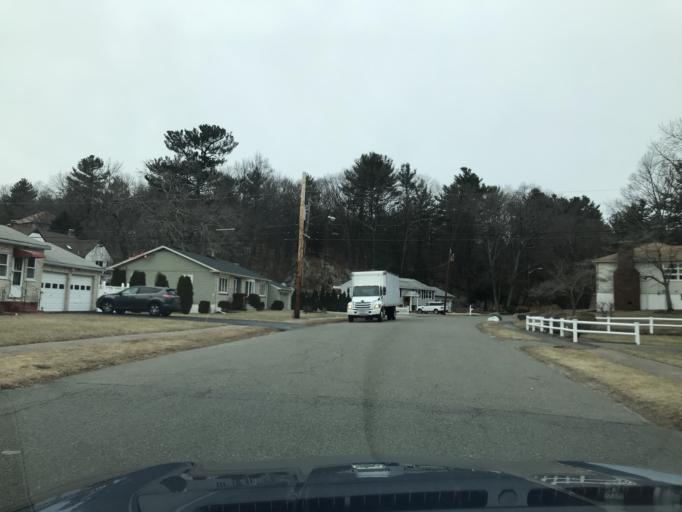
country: US
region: Massachusetts
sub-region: Essex County
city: Saugus
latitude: 42.4790
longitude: -71.0283
